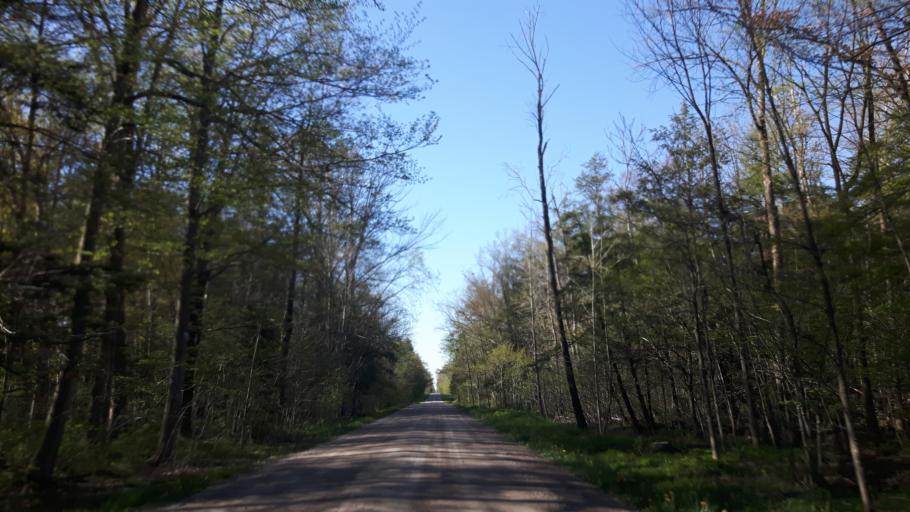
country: CA
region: Ontario
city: Bluewater
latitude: 43.5450
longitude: -81.5728
